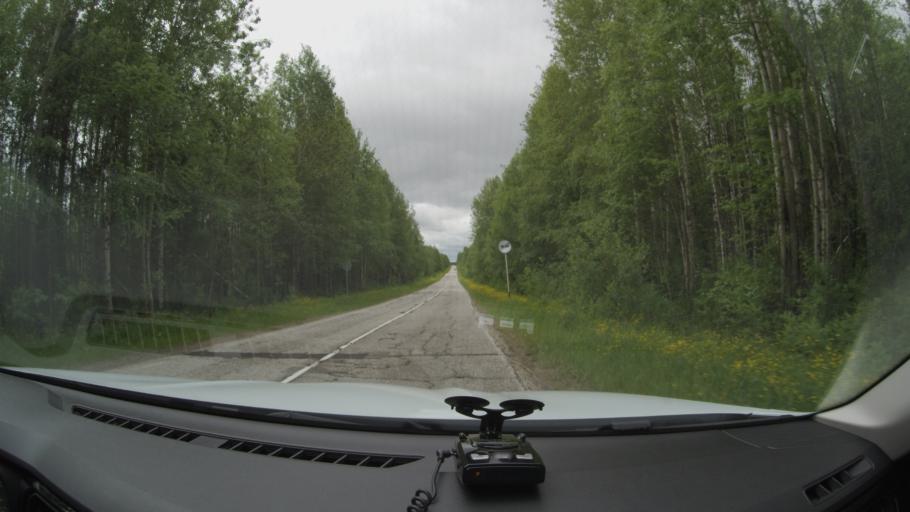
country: RU
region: Komi Republic
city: Nizhniy Odes
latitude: 63.6058
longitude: 54.5000
